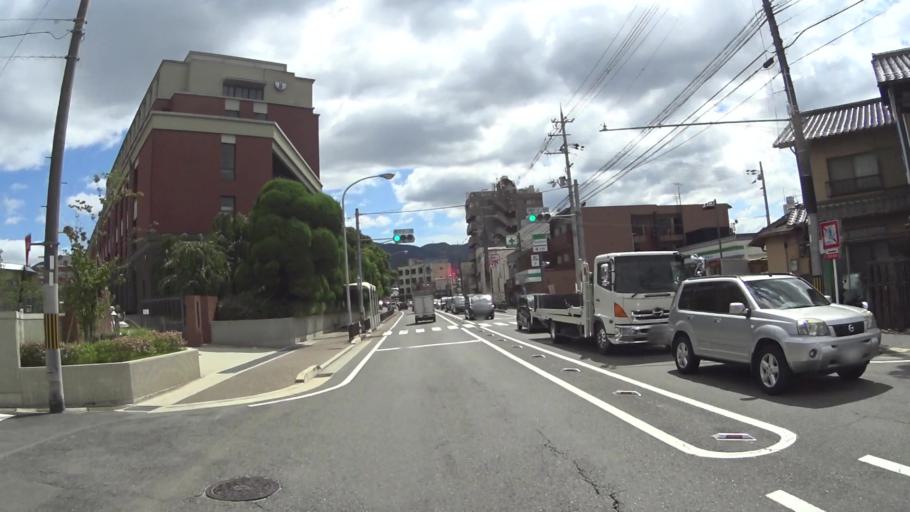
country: JP
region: Shiga Prefecture
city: Otsu-shi
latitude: 34.9910
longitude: 135.8087
